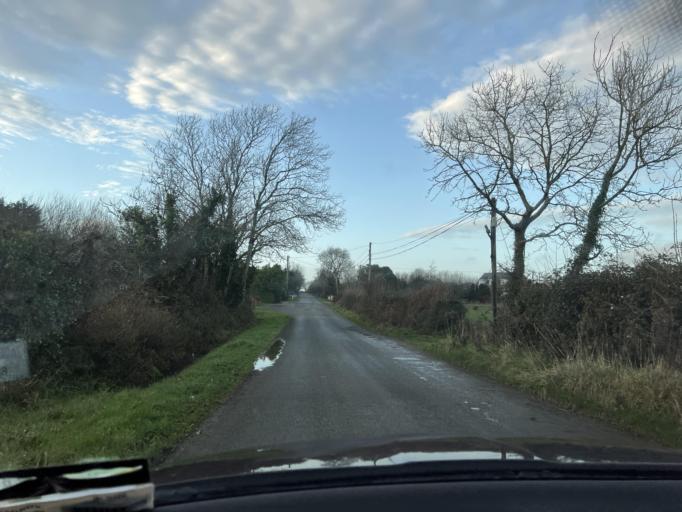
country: IE
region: Leinster
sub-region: Loch Garman
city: Loch Garman
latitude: 52.3616
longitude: -6.5221
